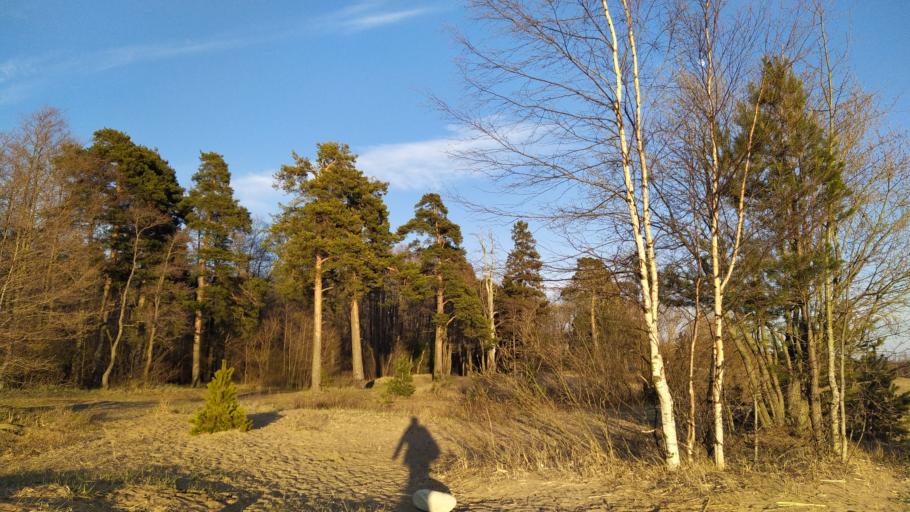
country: RU
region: St.-Petersburg
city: Tarkhovka
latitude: 60.0592
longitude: 29.9628
